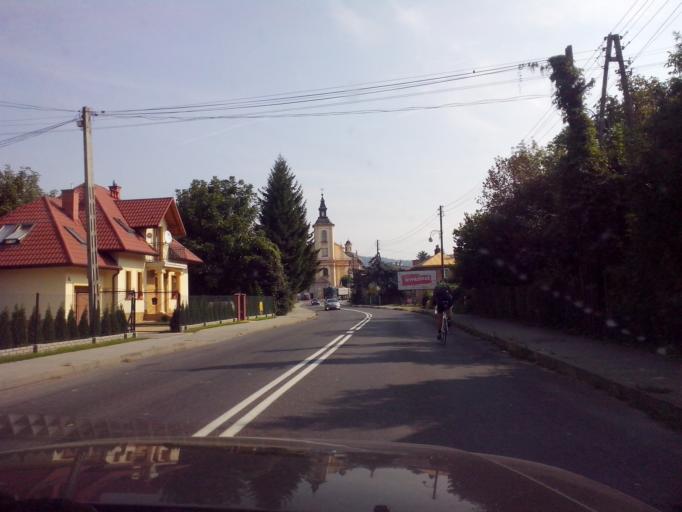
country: PL
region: Subcarpathian Voivodeship
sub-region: Powiat strzyzowski
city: Czudec
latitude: 49.9454
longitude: 21.8330
